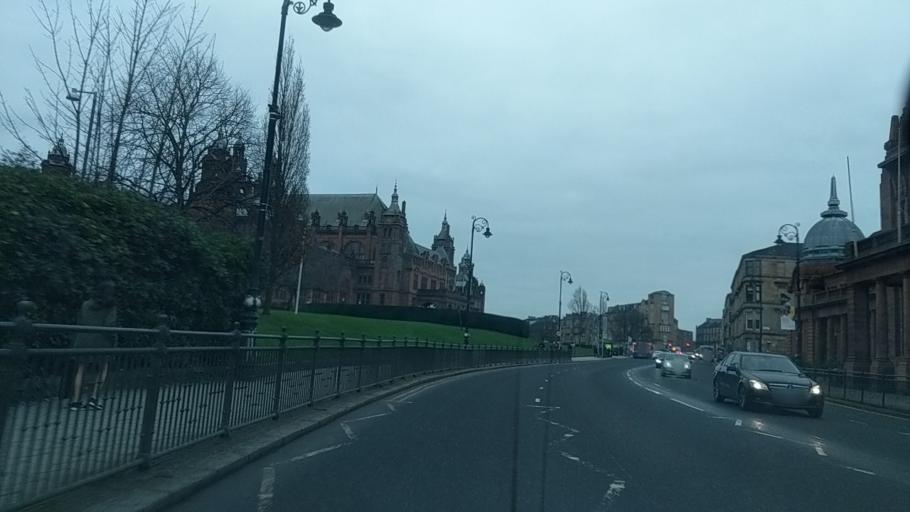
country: GB
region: Scotland
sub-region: Glasgow City
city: Glasgow
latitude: 55.8694
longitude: -4.2934
